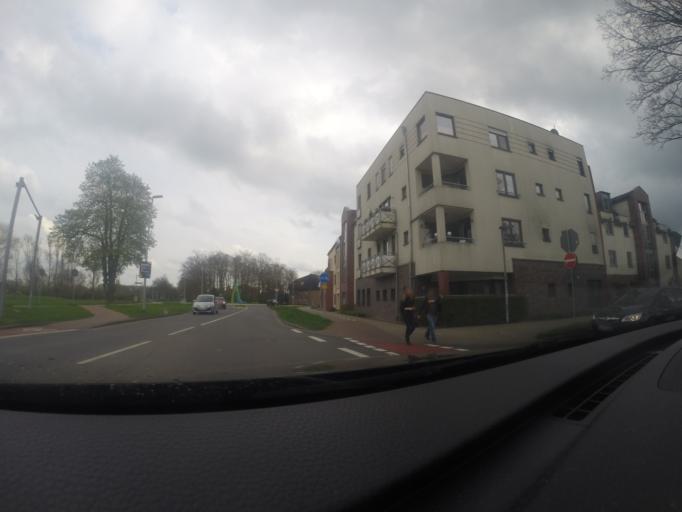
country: DE
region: North Rhine-Westphalia
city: Rheinberg
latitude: 51.5434
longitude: 6.6051
